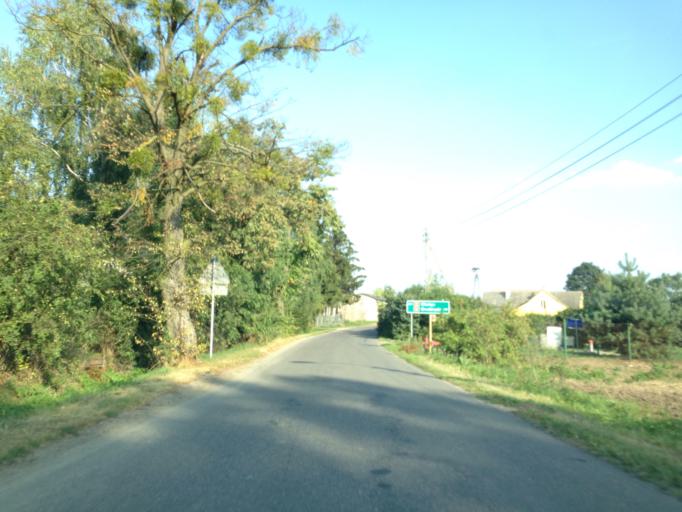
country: PL
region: Kujawsko-Pomorskie
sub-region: Powiat grudziadzki
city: Lasin
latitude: 53.5427
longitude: 19.1337
